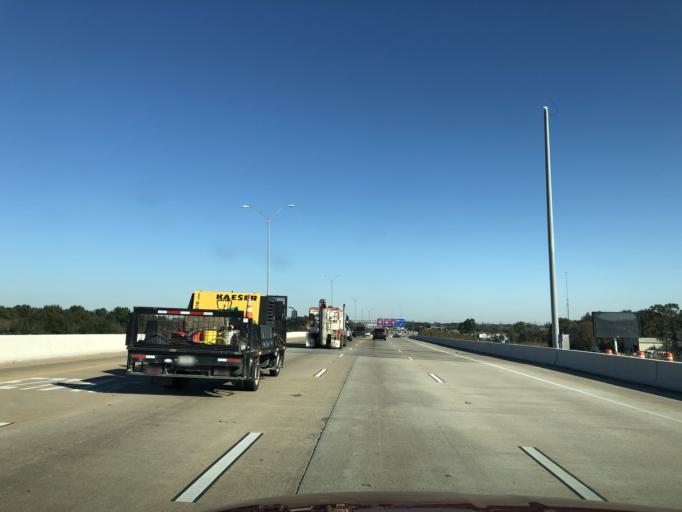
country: US
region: Texas
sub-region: Fort Bend County
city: Fresno
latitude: 29.5970
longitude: -95.4259
